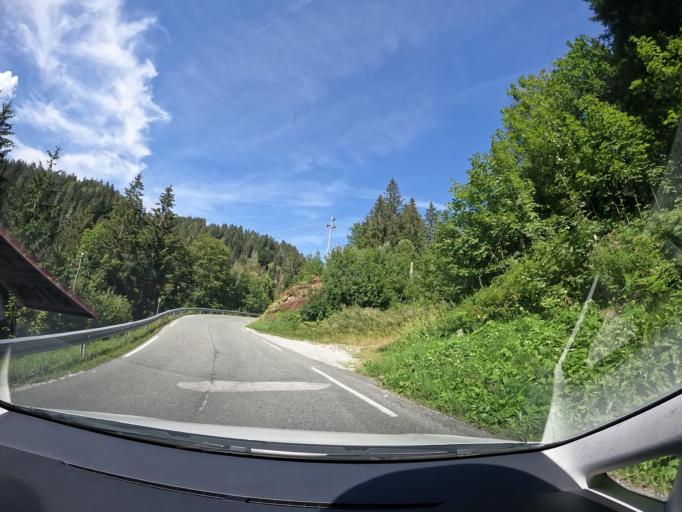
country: AT
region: Carinthia
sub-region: Politischer Bezirk Villach Land
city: Sankt Jakob
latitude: 46.5513
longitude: 14.0796
